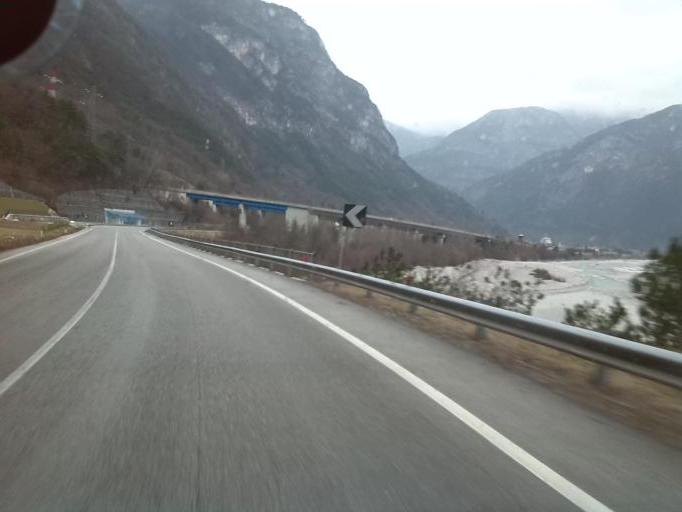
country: IT
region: Friuli Venezia Giulia
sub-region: Provincia di Udine
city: Chiusaforte
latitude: 46.3986
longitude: 13.2834
